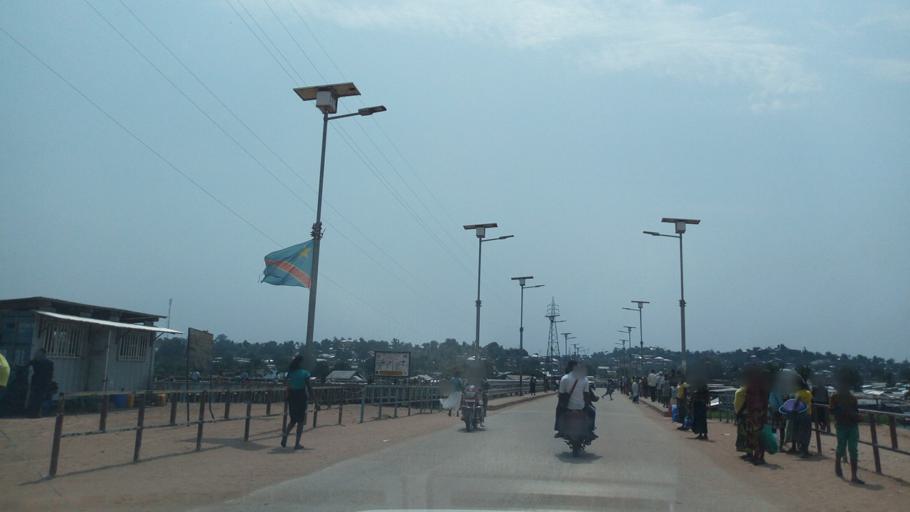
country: CD
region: Katanga
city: Kalemie
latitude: -5.9140
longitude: 29.1900
